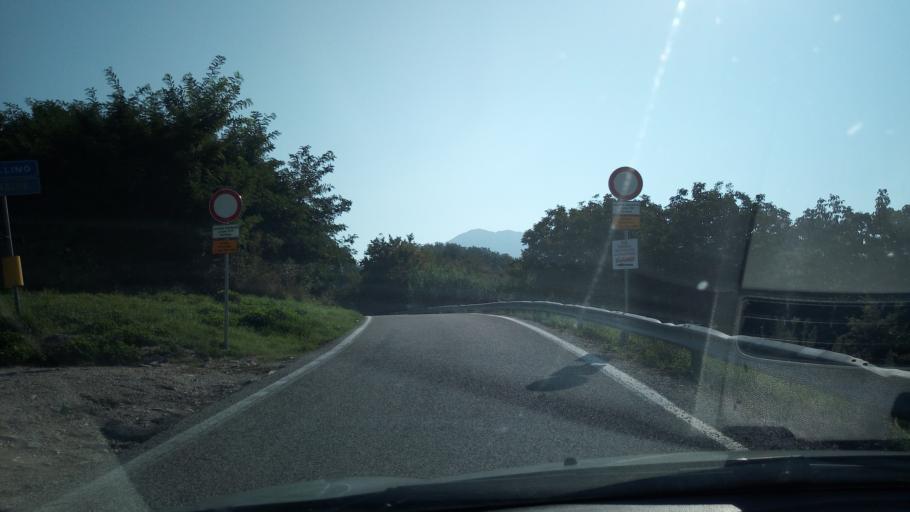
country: IT
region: Campania
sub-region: Provincia di Avellino
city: San Potito Ultra
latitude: 40.9286
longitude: 14.8616
